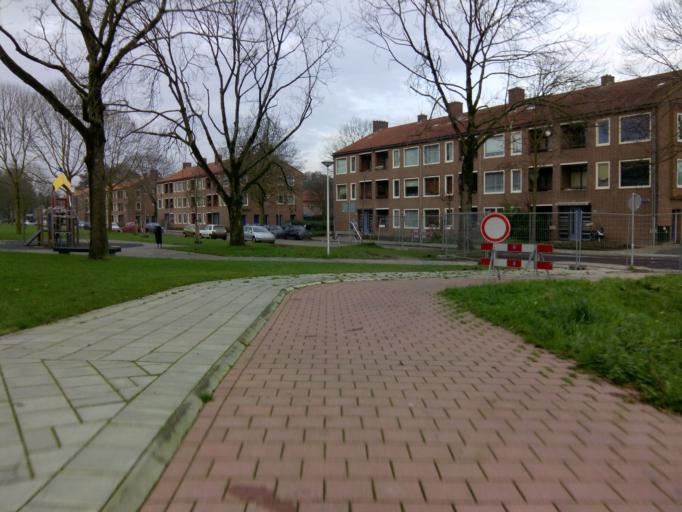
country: NL
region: Utrecht
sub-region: Gemeente Amersfoort
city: Randenbroek
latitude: 52.1467
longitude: 5.4096
